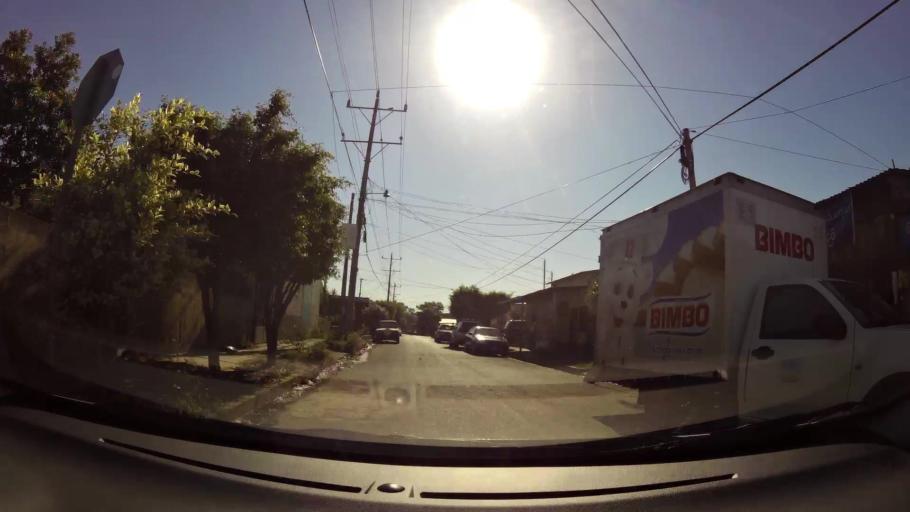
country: SV
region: Sonsonate
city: Sonzacate
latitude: 13.7425
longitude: -89.7140
